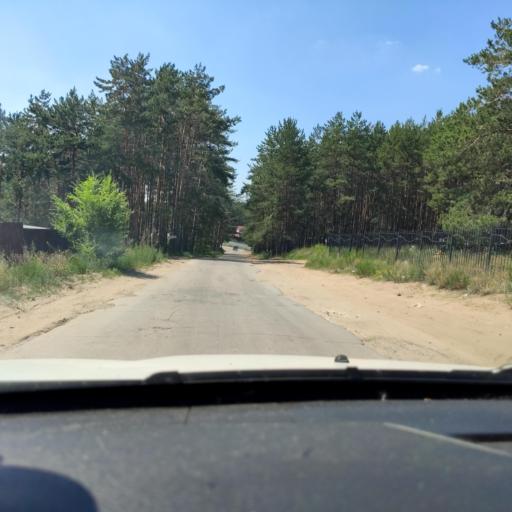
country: RU
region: Samara
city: Pribrezhnyy
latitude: 53.4824
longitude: 49.8376
